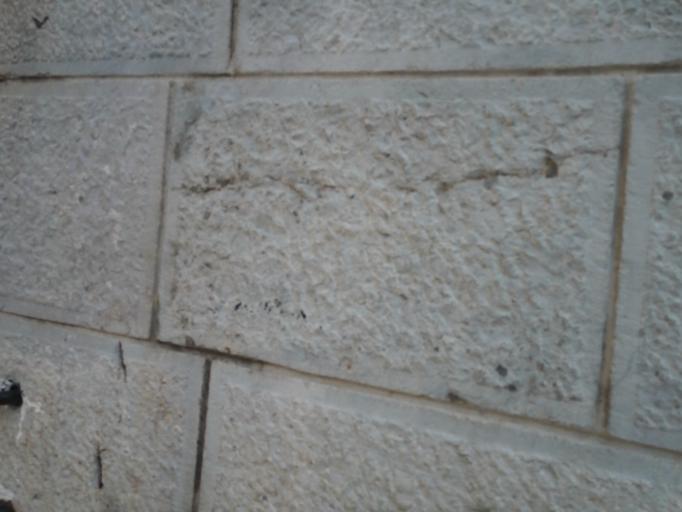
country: DZ
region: Constantine
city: Constantine
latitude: 36.3720
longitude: 6.6137
